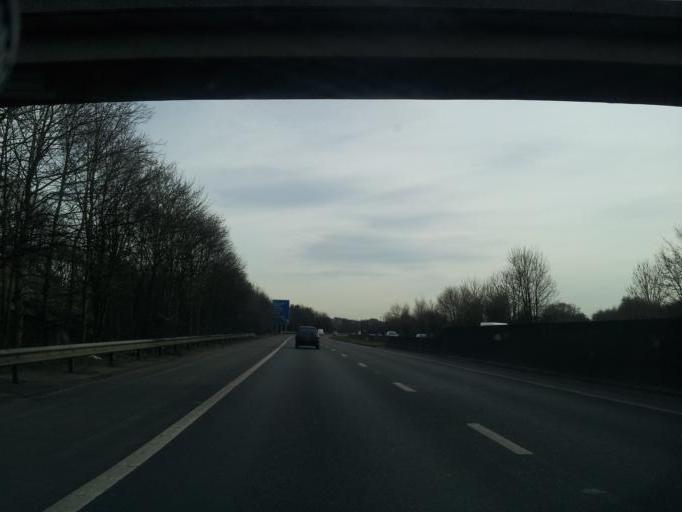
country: GB
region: England
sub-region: Hertfordshire
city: Potters Bar
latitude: 51.7133
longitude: -0.2221
